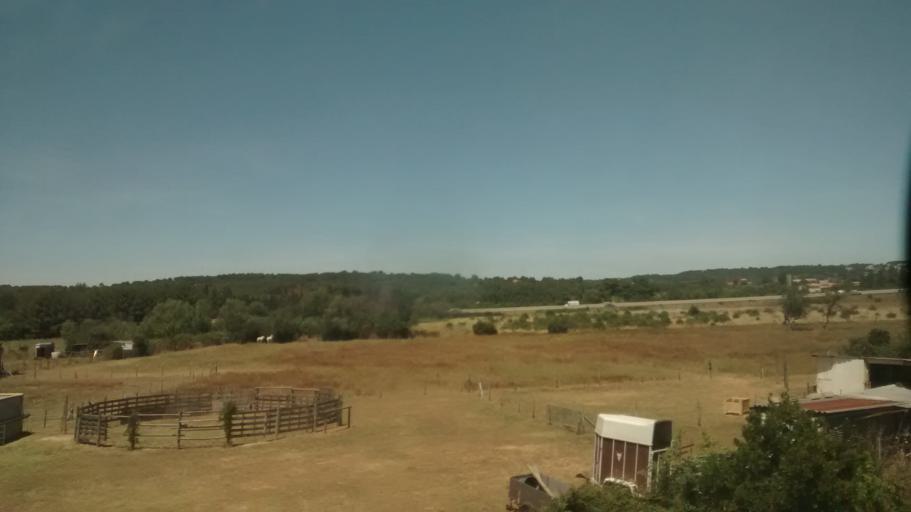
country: FR
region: Languedoc-Roussillon
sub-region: Departement du Gard
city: Milhaud
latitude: 43.7977
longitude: 4.3127
